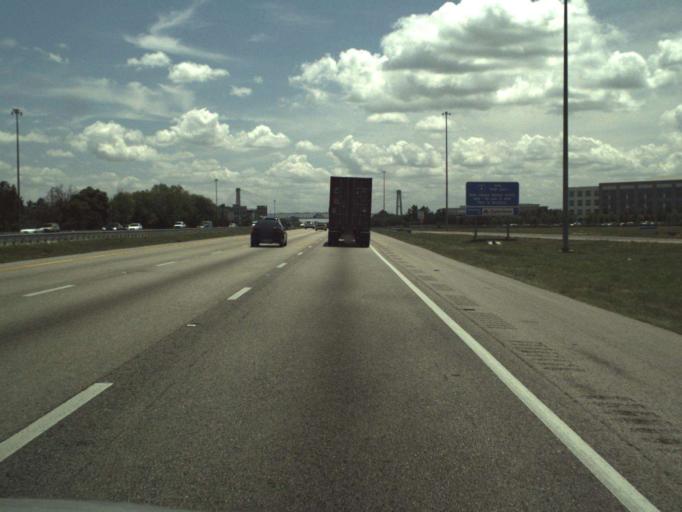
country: US
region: Florida
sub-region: Seminole County
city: Heathrow
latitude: 28.7844
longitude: -81.3517
